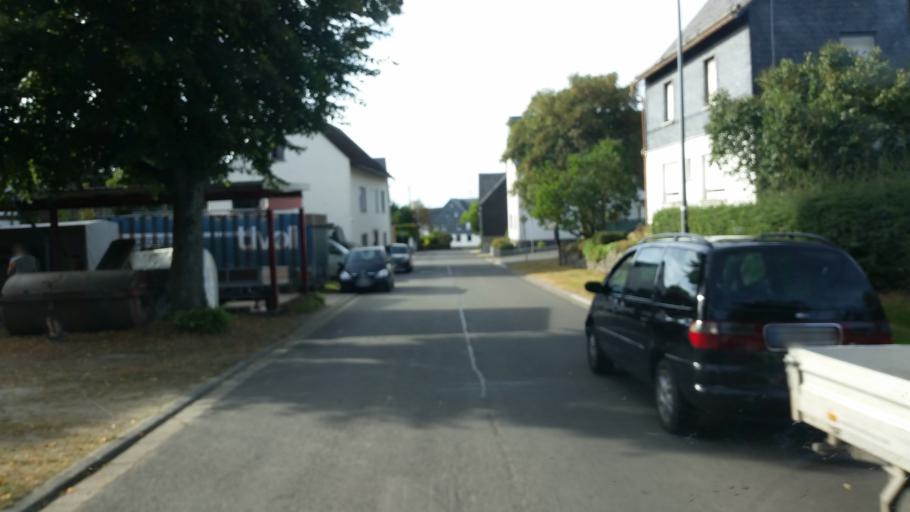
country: DE
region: Rheinland-Pfalz
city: Raversbeuren
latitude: 49.9546
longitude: 7.2292
